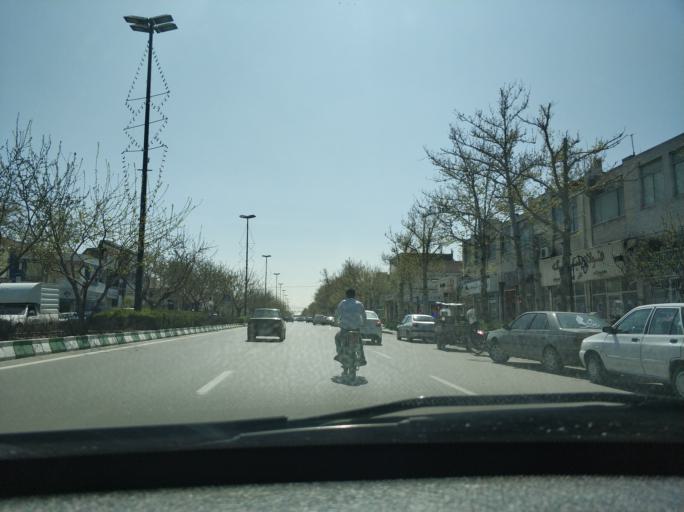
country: IR
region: Razavi Khorasan
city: Mashhad
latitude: 36.2655
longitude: 59.6012
